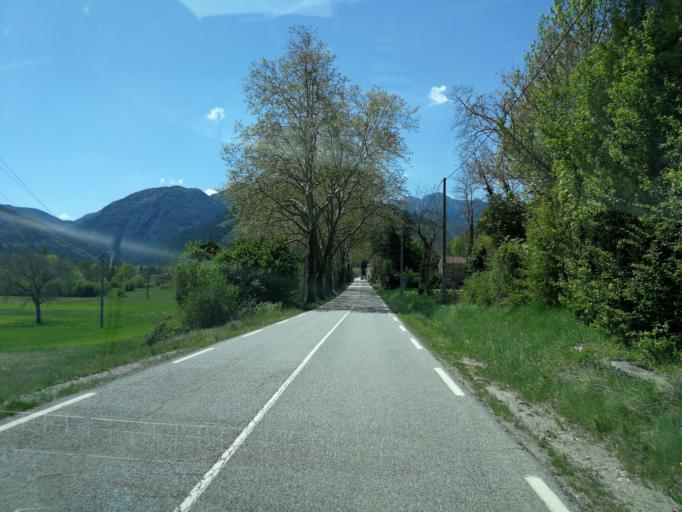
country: FR
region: Rhone-Alpes
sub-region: Departement de la Drome
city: Die
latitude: 44.7106
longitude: 5.2629
